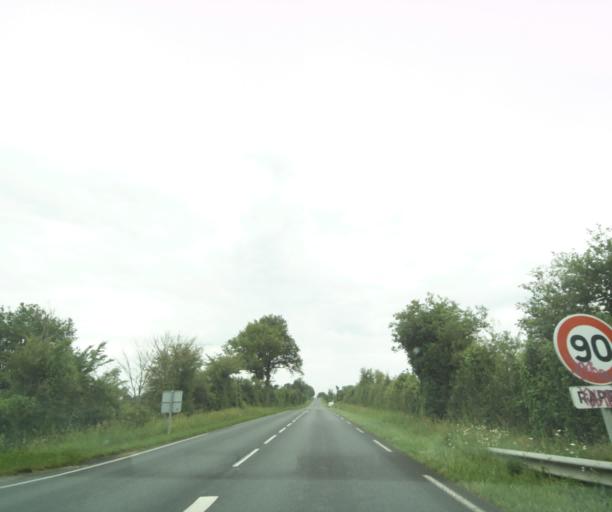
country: FR
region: Poitou-Charentes
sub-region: Departement des Deux-Sevres
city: Viennay
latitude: 46.7192
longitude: -0.2387
